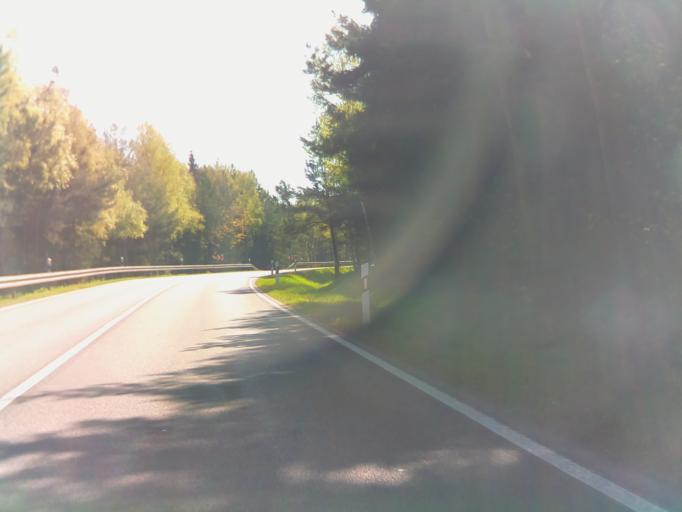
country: DE
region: Saxony
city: Pausa
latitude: 50.5468
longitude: 11.9841
